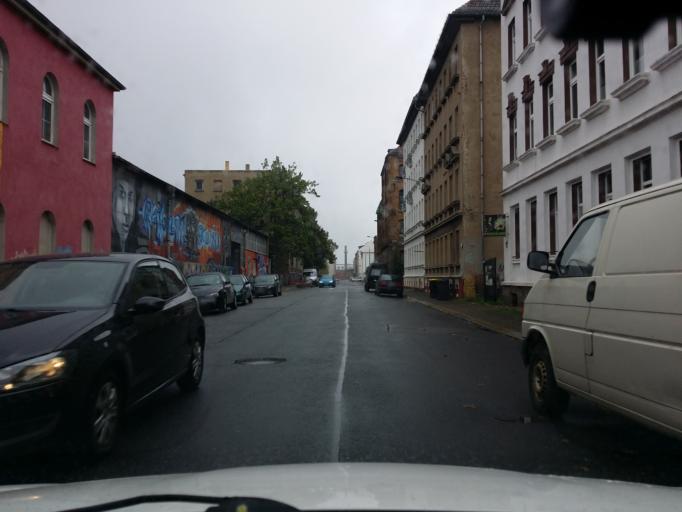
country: DE
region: Saxony
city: Leipzig
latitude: 51.3226
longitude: 12.3246
